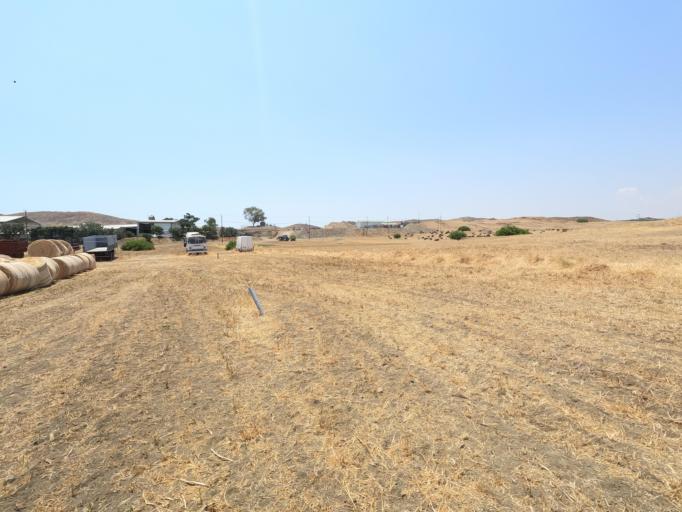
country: CY
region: Larnaka
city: Troulloi
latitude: 35.0122
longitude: 33.6203
